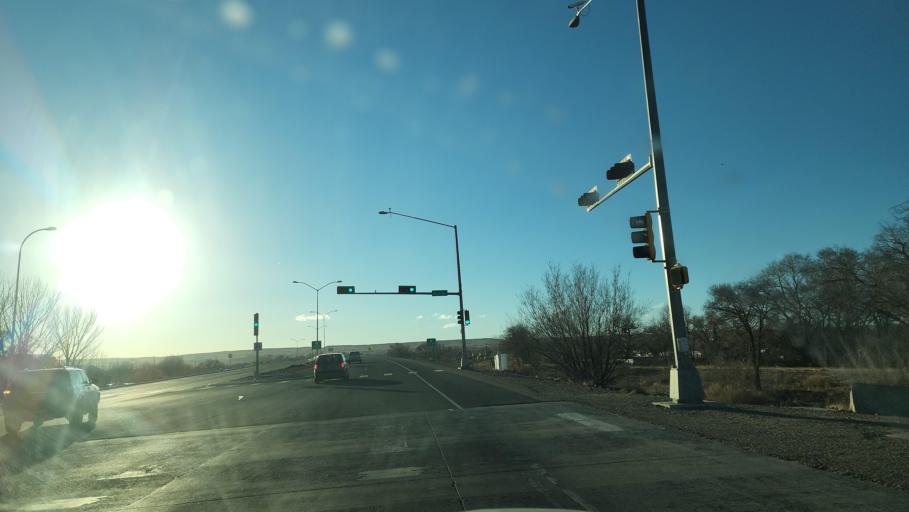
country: US
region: New Mexico
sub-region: Bernalillo County
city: South Valley
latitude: 35.0278
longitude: -106.7091
